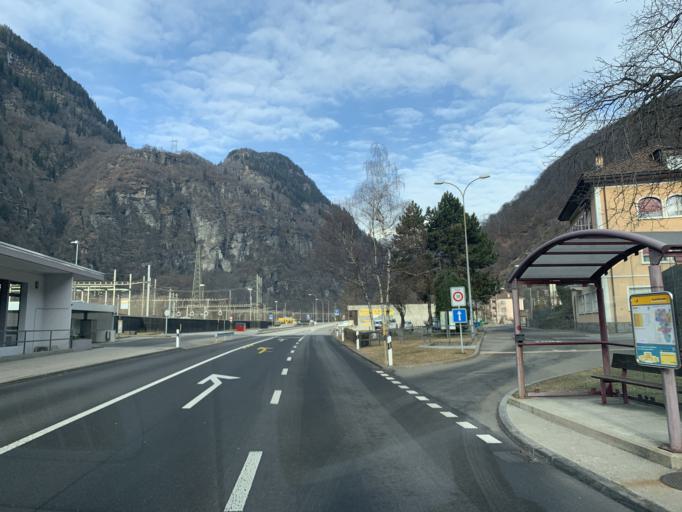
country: CH
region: Ticino
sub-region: Leventina District
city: Faido
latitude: 46.4410
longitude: 8.8400
